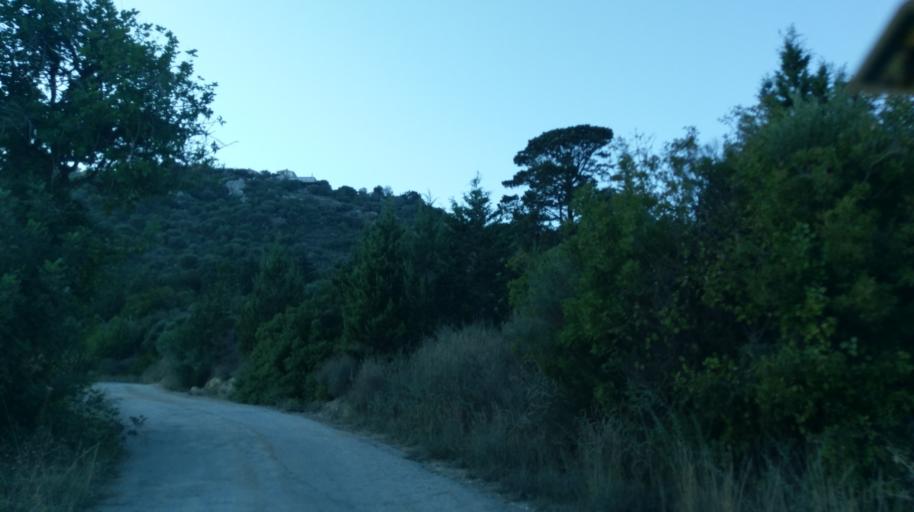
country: CY
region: Ammochostos
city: Trikomo
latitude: 35.3840
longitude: 33.9028
